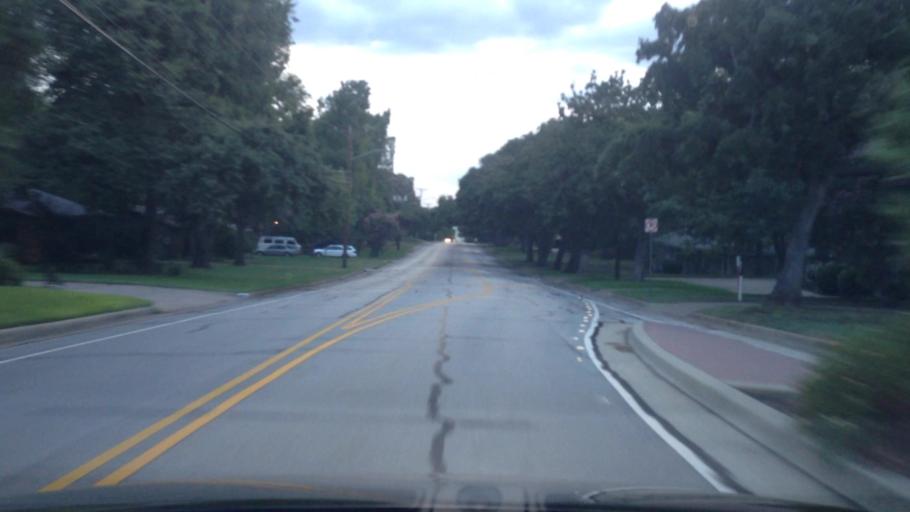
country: US
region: Texas
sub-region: Tarrant County
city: Arlington
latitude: 32.7317
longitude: -97.1327
